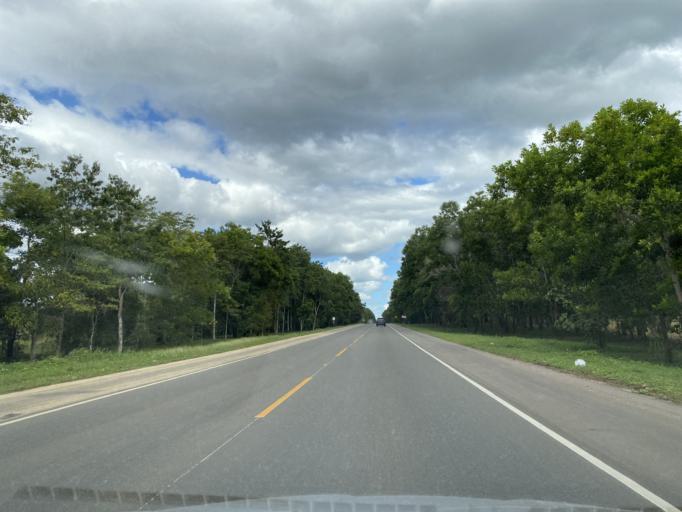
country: DO
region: Santo Domingo
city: Guerra
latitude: 18.6357
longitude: -69.7578
